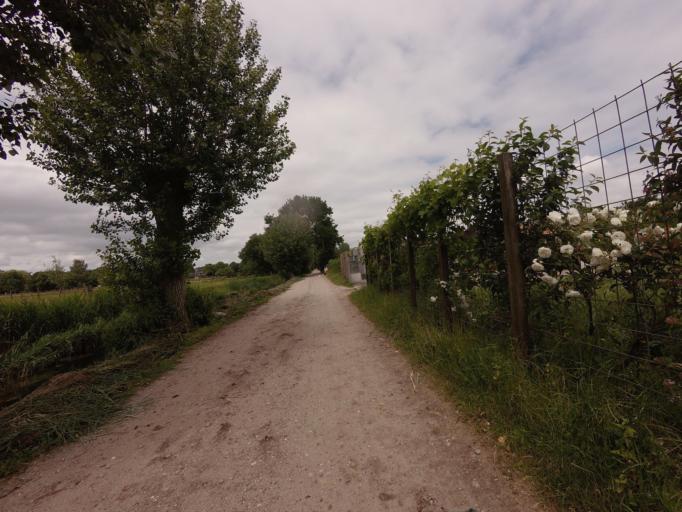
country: NL
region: North Holland
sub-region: Gemeente Blaricum
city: Blaricum
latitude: 52.2675
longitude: 5.2545
